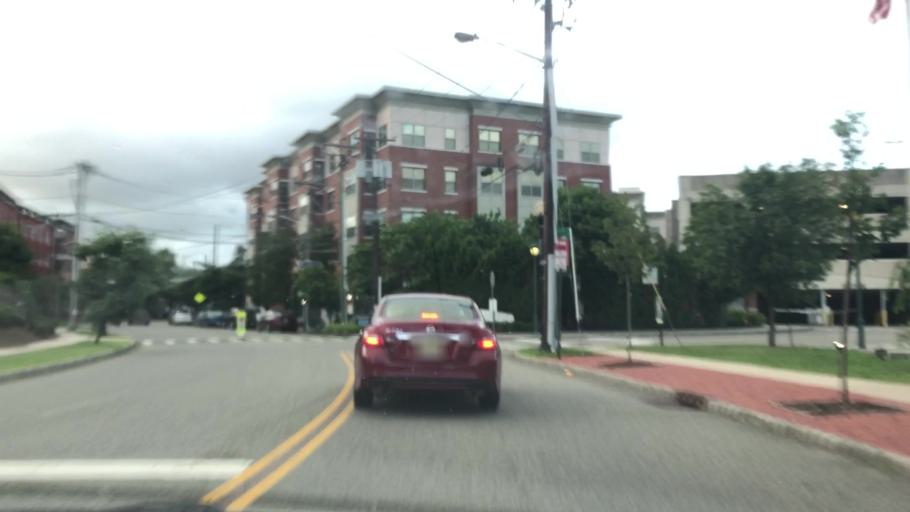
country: US
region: New Jersey
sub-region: Essex County
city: Glen Ridge
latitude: 40.8077
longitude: -74.2097
